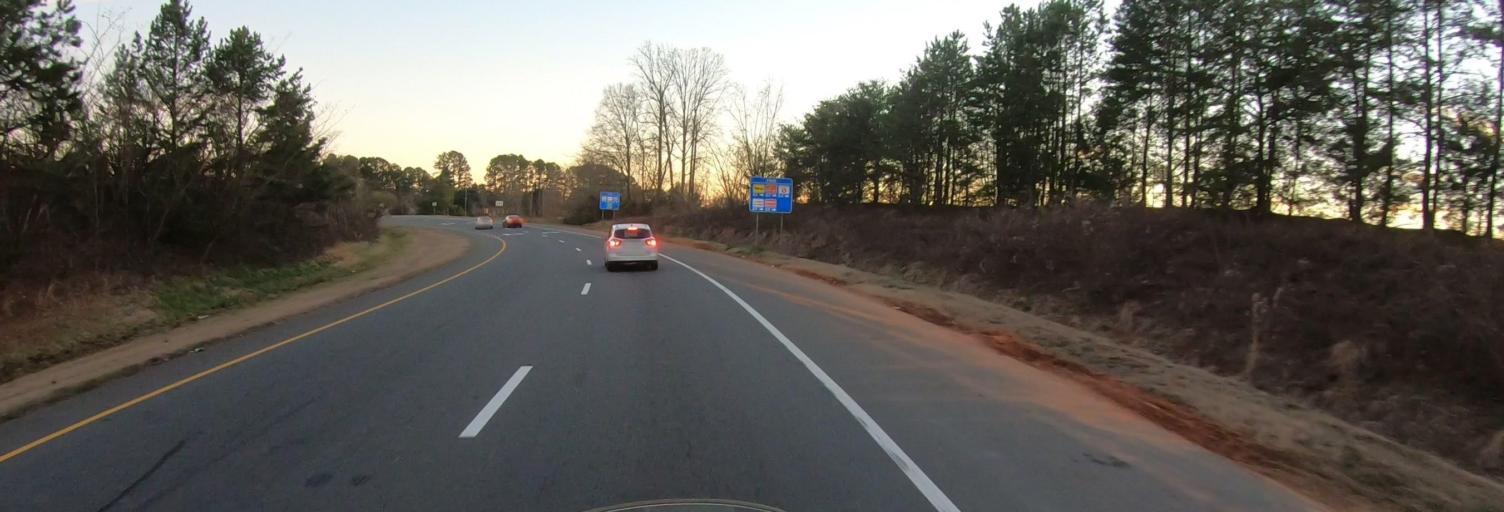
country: US
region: South Carolina
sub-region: York County
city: Lake Wylie
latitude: 35.1674
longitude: -80.9682
